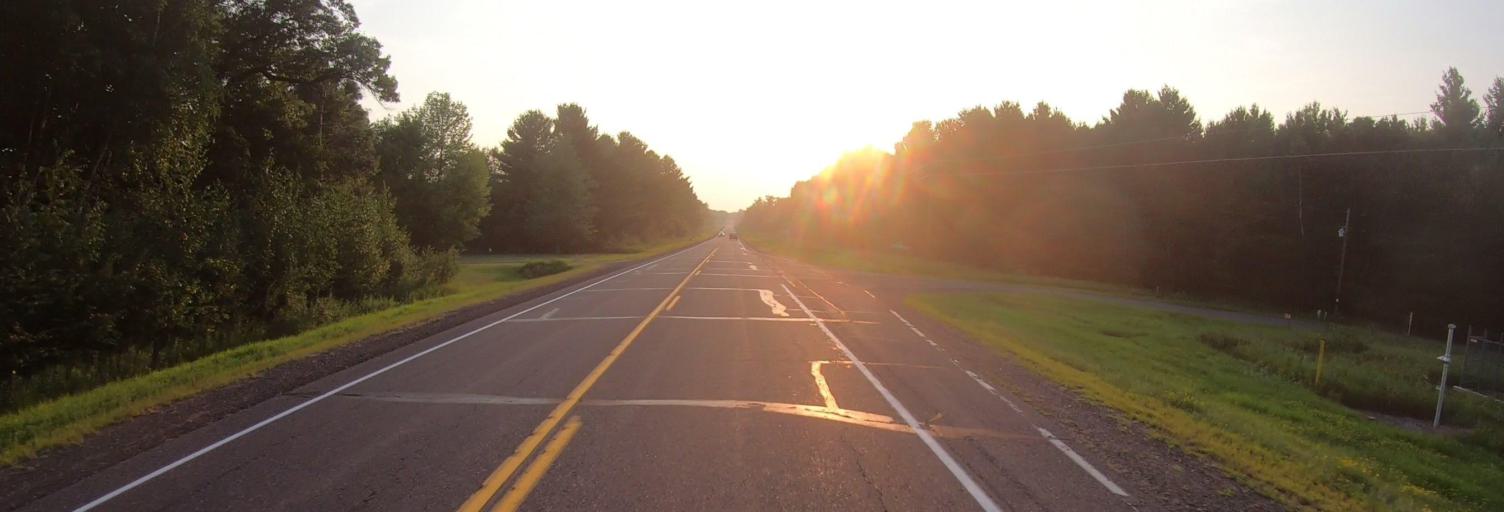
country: US
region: Wisconsin
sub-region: Burnett County
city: Siren
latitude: 45.7697
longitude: -92.4876
